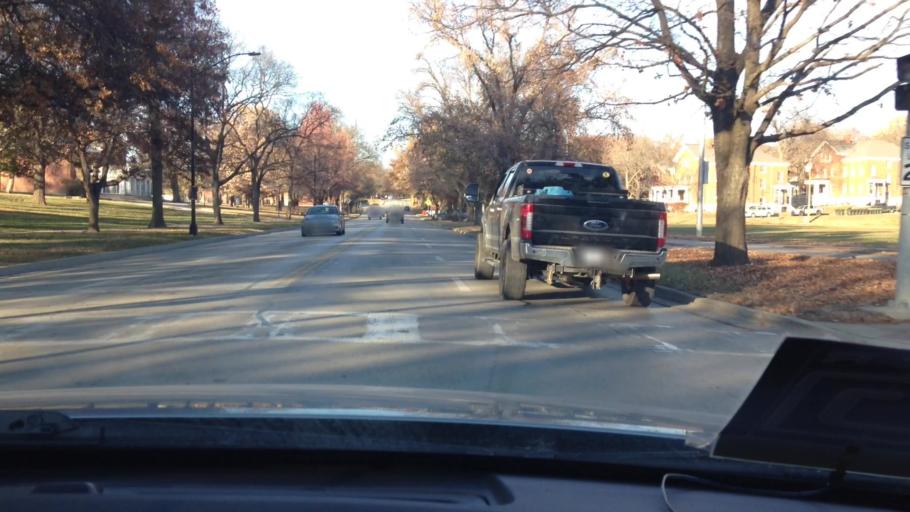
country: US
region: Kansas
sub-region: Leavenworth County
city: Leavenworth
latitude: 39.3487
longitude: -94.9191
